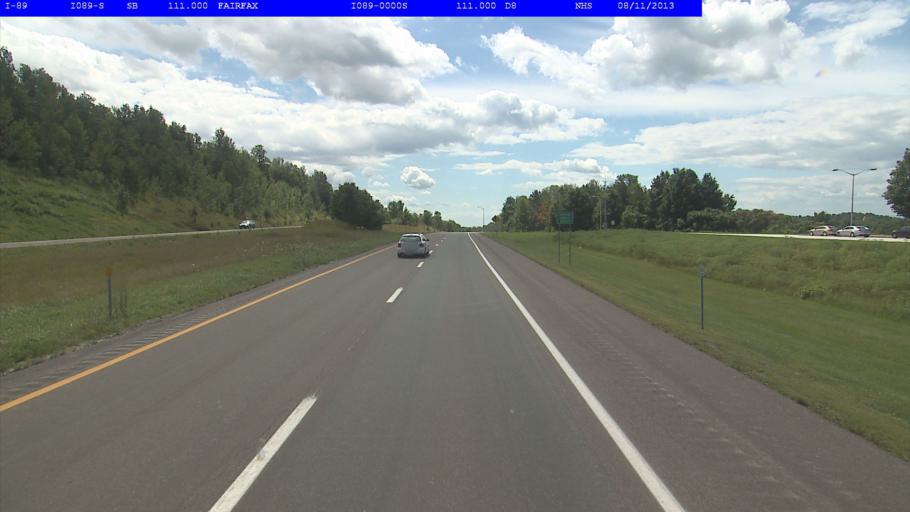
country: US
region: Vermont
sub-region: Franklin County
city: Saint Albans
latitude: 44.7556
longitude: -73.0776
